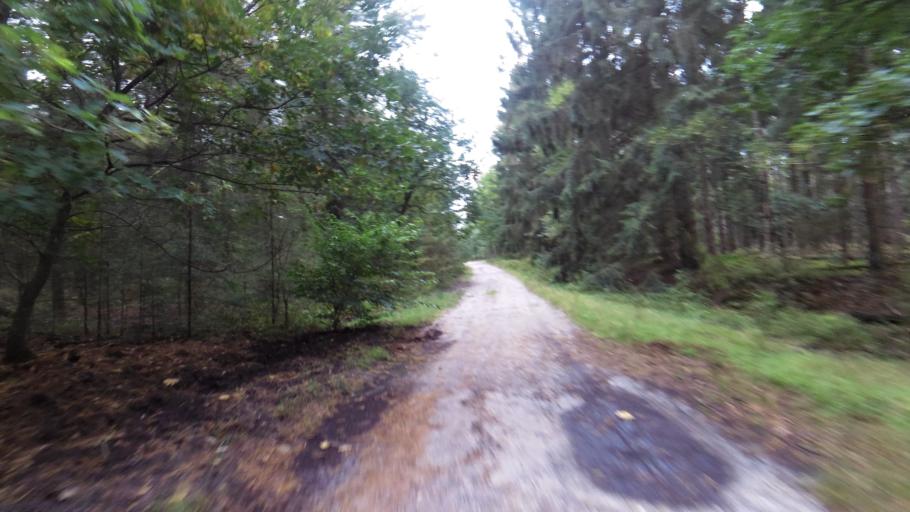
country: NL
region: Gelderland
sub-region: Gemeente Apeldoorn
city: Beekbergen
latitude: 52.1893
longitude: 5.9005
